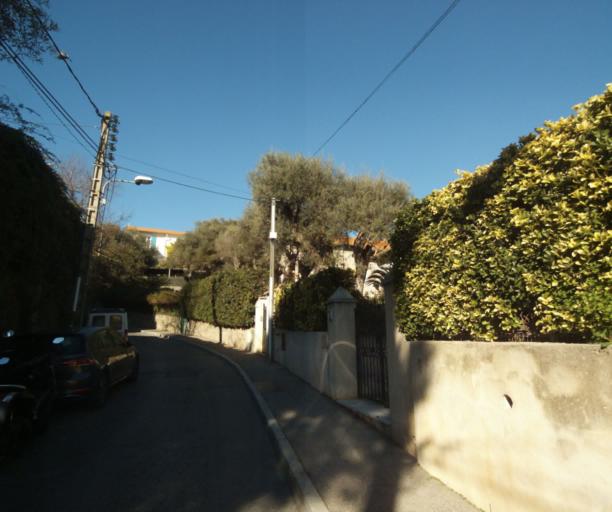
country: FR
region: Provence-Alpes-Cote d'Azur
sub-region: Departement des Alpes-Maritimes
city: Antibes
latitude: 43.5776
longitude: 7.1141
